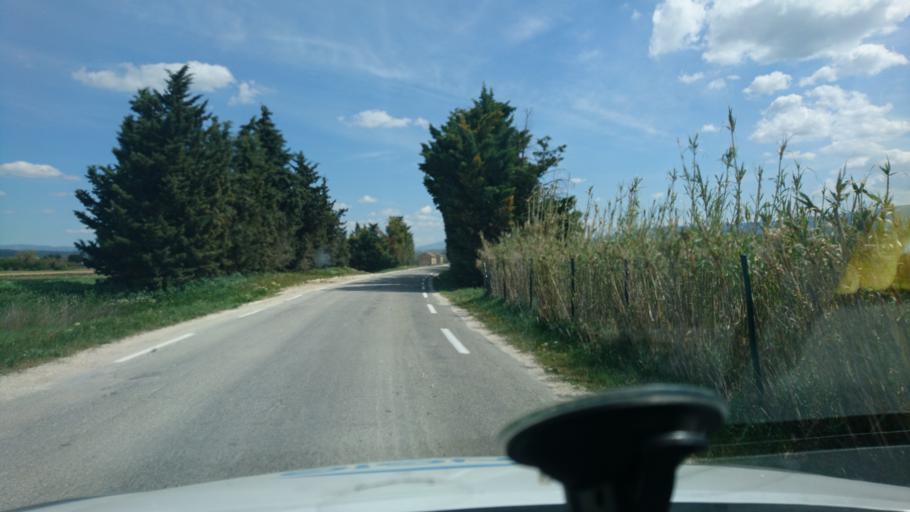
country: FR
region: Provence-Alpes-Cote d'Azur
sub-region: Departement du Vaucluse
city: Maubec
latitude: 43.8605
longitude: 5.1392
